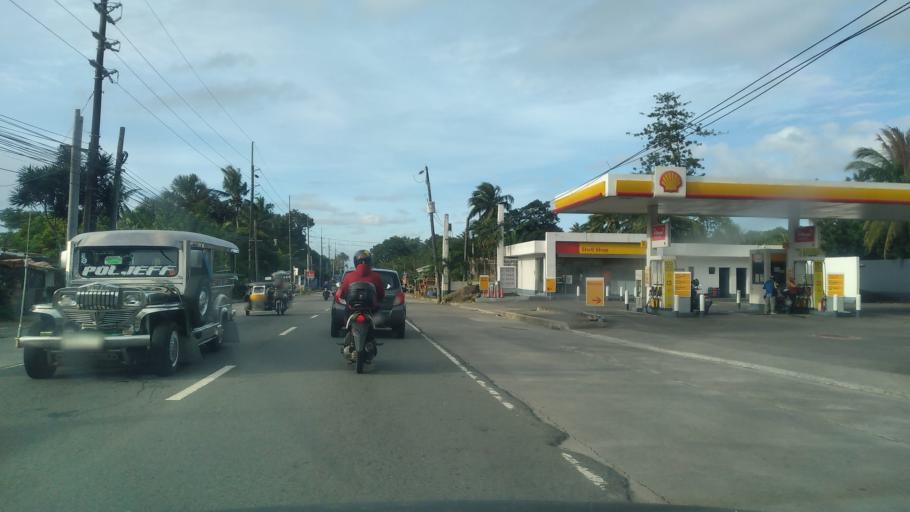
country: PH
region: Calabarzon
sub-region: Province of Quezon
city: Calumpang
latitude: 13.9719
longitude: 121.5529
